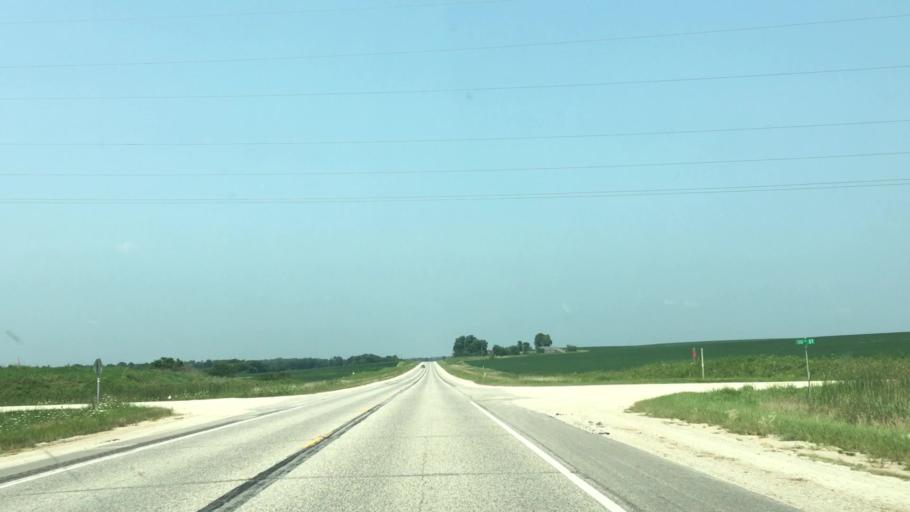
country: US
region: Iowa
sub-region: Fayette County
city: Fayette
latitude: 42.7884
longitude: -91.8048
